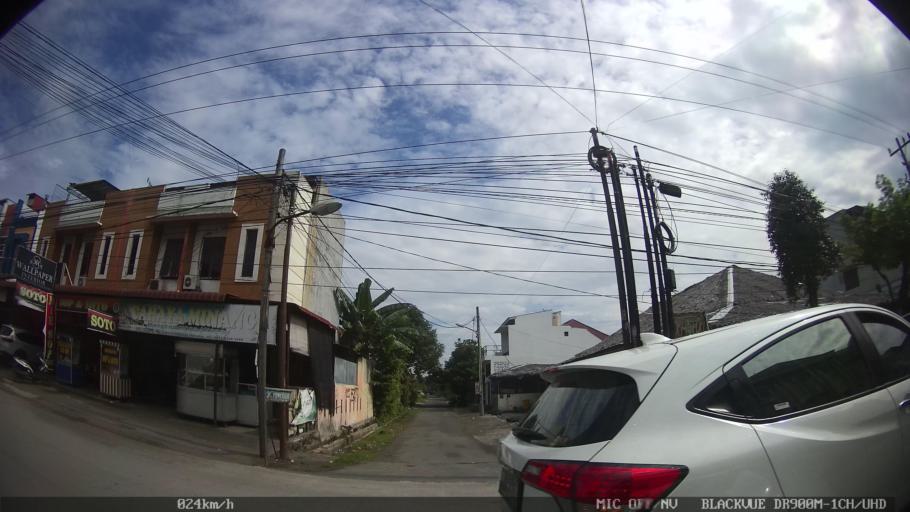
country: ID
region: North Sumatra
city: Sunggal
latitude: 3.6065
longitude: 98.6137
